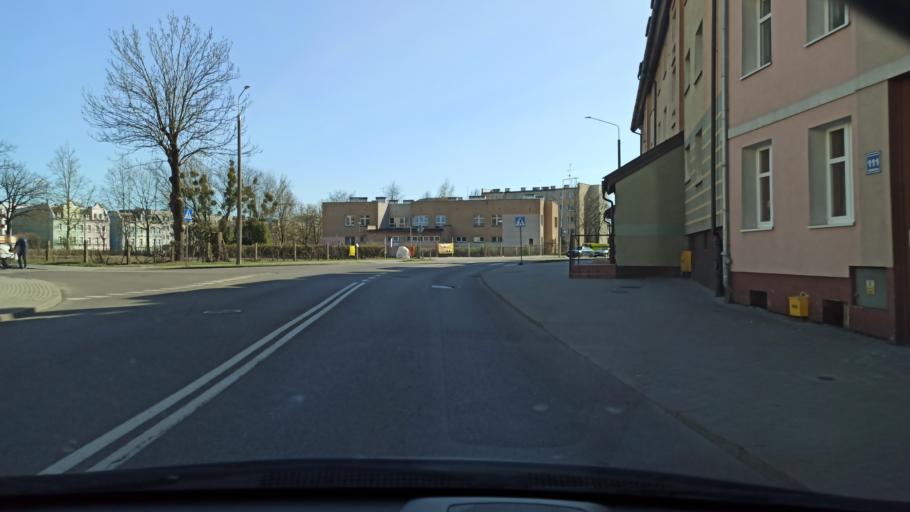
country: PL
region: Warmian-Masurian Voivodeship
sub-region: Powiat elblaski
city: Elblag
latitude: 54.1731
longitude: 19.4032
